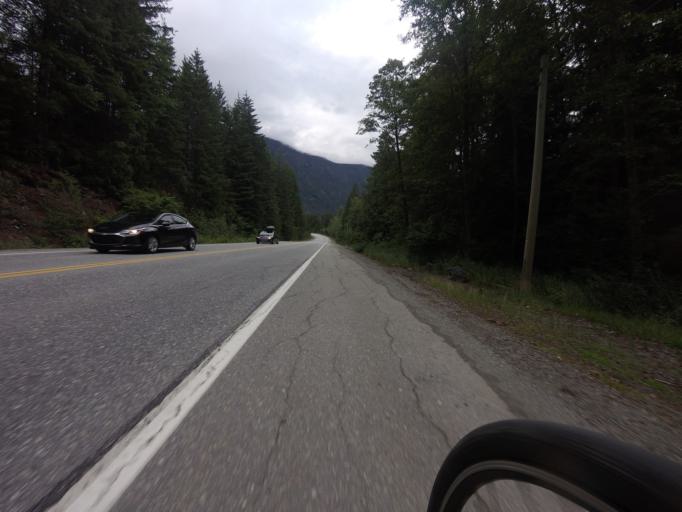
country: CA
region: British Columbia
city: Pemberton
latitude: 50.2604
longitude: -122.8649
